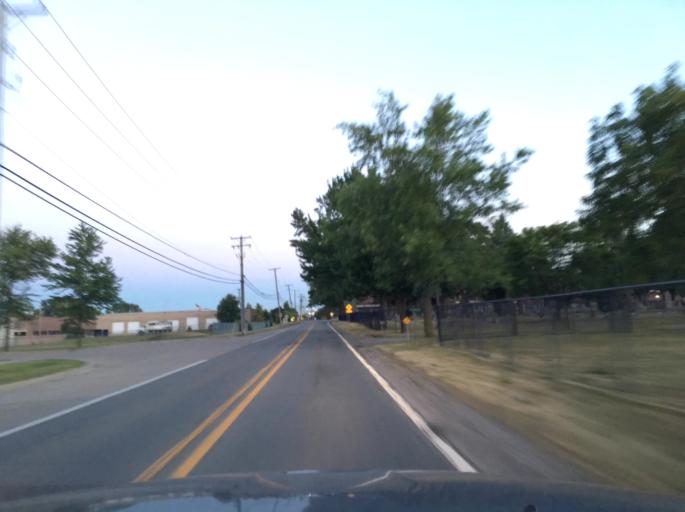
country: US
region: Michigan
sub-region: Macomb County
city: Mount Clemens
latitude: 42.6200
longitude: -82.8879
